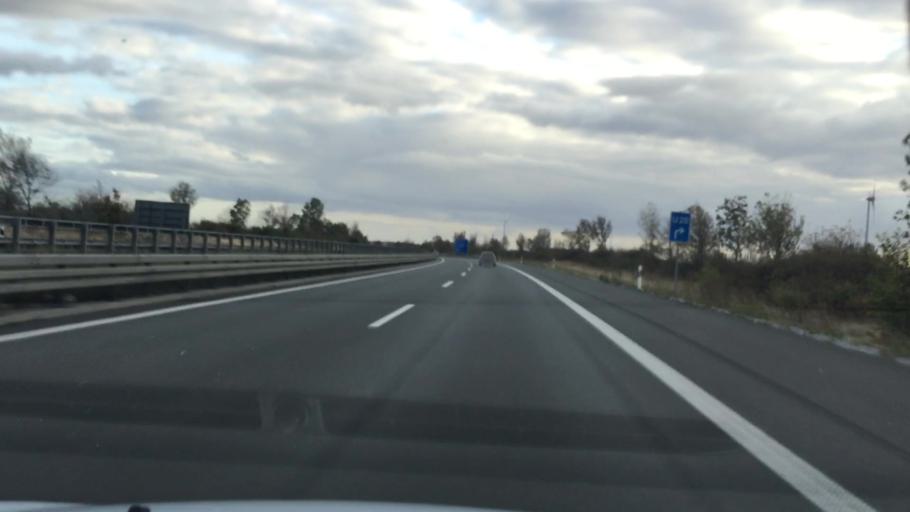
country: DE
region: Saxony-Anhalt
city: Plotzkau
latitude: 51.7447
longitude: 11.6662
